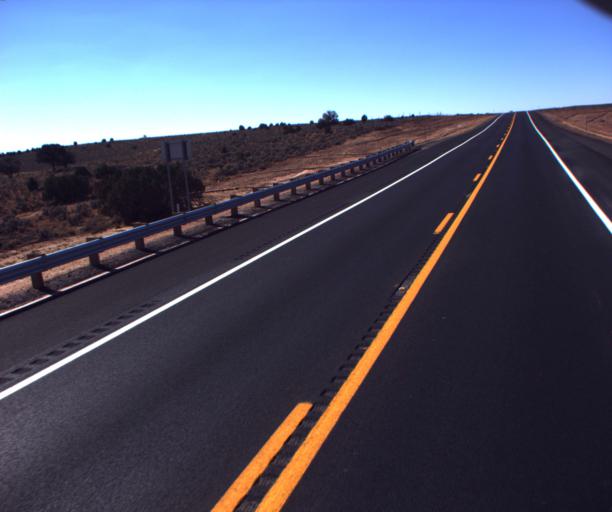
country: US
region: Arizona
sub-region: Apache County
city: Ganado
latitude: 35.7182
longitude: -109.4647
